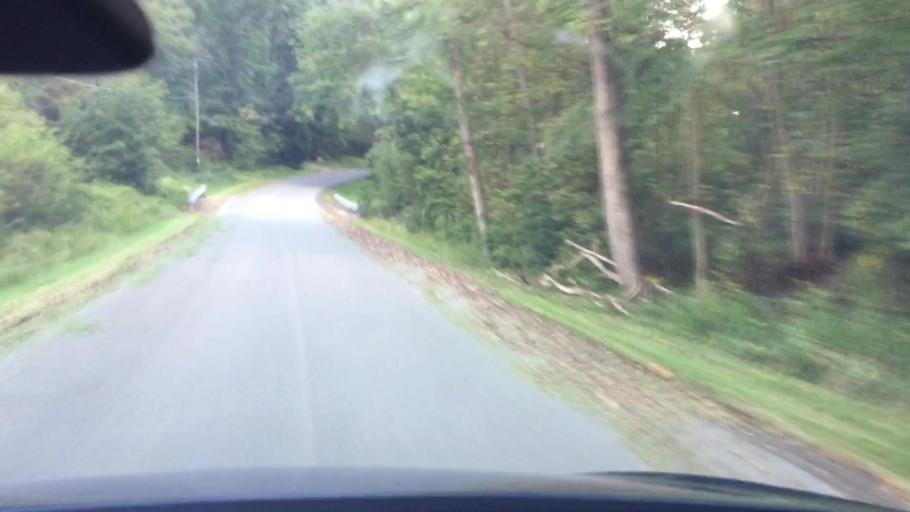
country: US
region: Pennsylvania
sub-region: Butler County
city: Oak Hills
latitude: 40.7913
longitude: -79.8867
